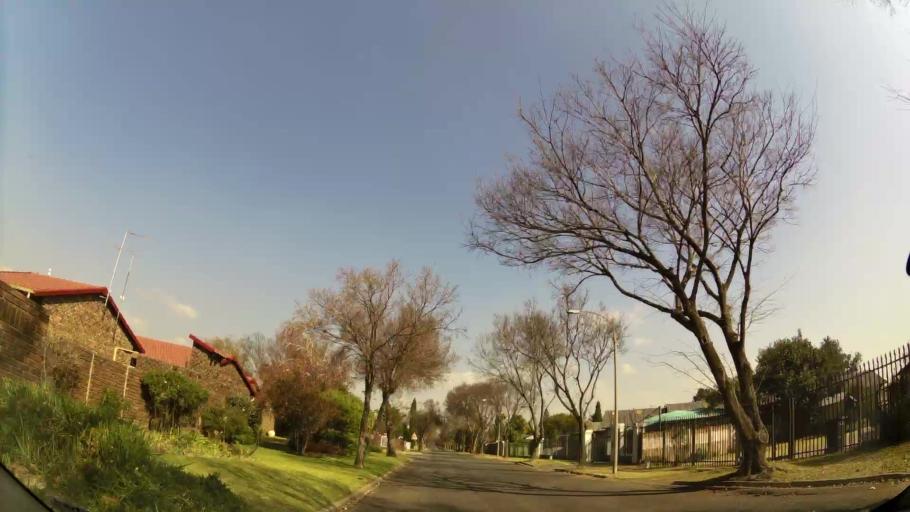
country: ZA
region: Gauteng
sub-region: Ekurhuleni Metropolitan Municipality
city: Benoni
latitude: -26.1520
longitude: 28.2807
